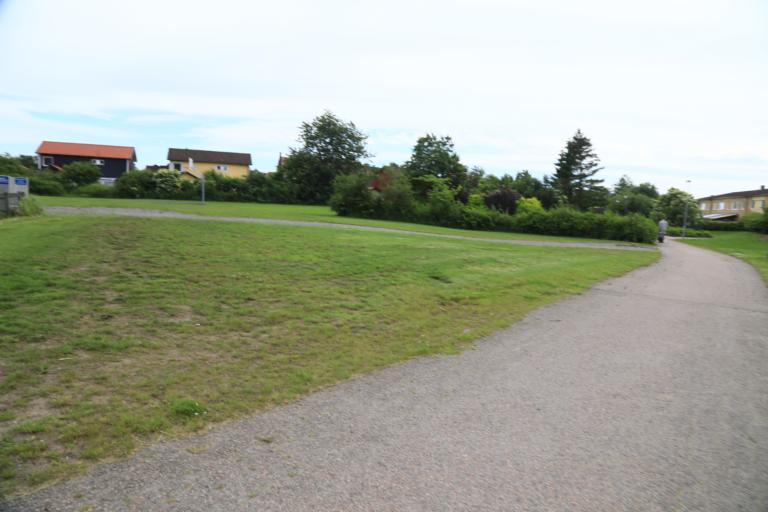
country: SE
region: Halland
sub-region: Varbergs Kommun
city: Varberg
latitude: 57.1132
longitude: 12.2727
